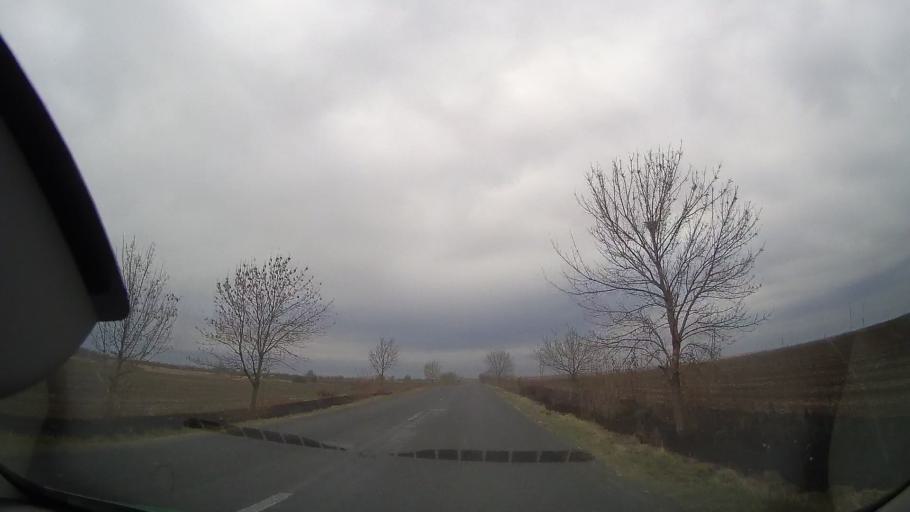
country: RO
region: Buzau
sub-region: Comuna Padina
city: Padina
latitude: 44.7832
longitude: 27.1501
